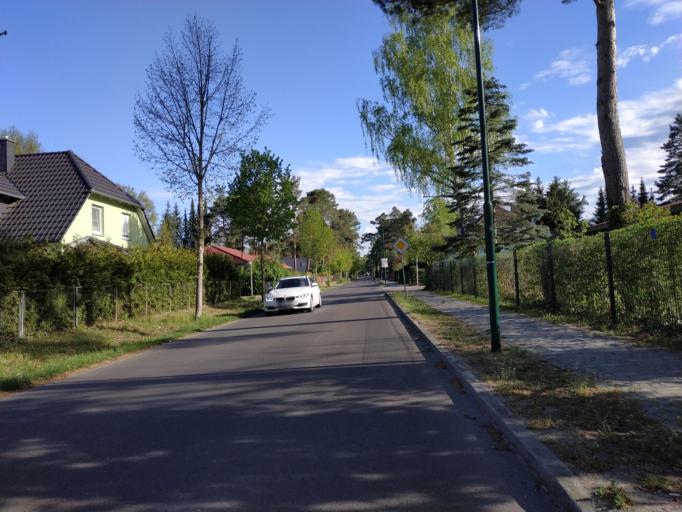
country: DE
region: Brandenburg
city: Petershagen
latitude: 52.5443
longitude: 13.8267
